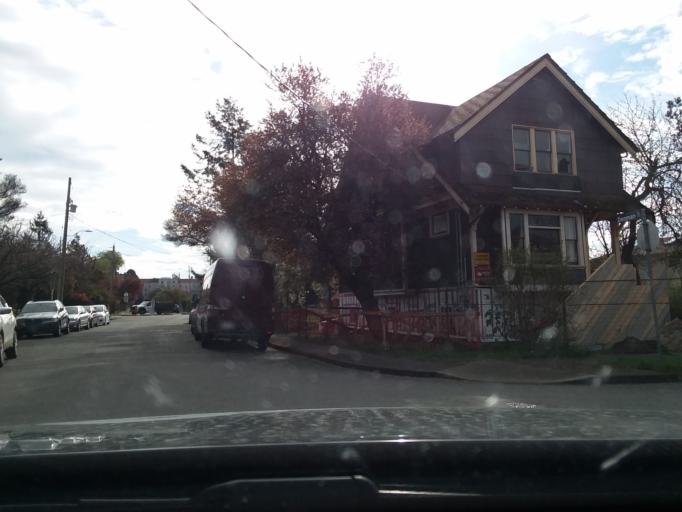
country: CA
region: British Columbia
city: Victoria
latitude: 48.4326
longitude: -123.3343
